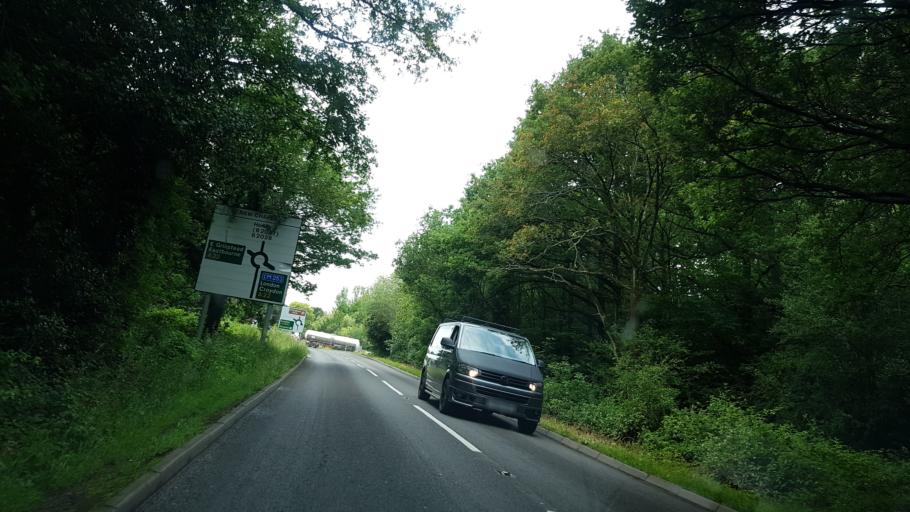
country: GB
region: England
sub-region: Surrey
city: Felbridge
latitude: 51.1650
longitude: -0.0485
